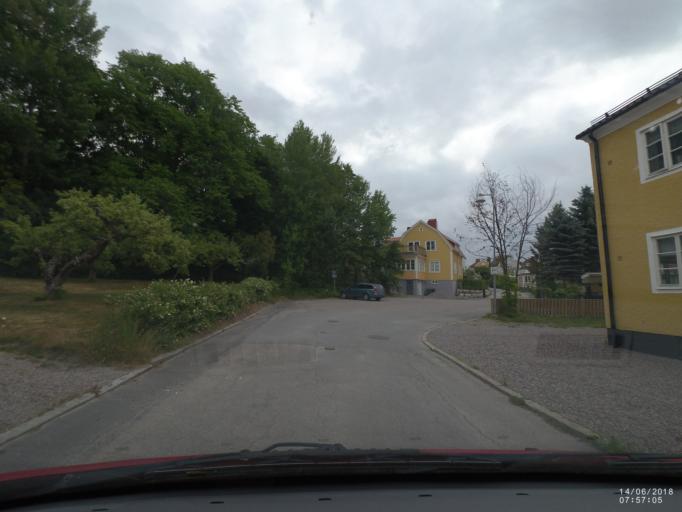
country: SE
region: Soedermanland
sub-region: Nykopings Kommun
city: Nykoping
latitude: 58.7581
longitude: 17.0223
